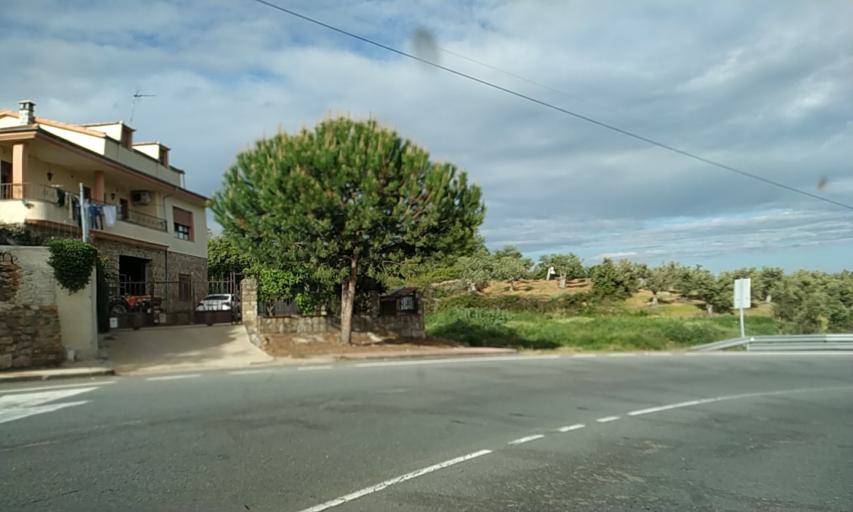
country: ES
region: Extremadura
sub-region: Provincia de Caceres
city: Perales del Puerto
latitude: 40.1541
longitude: -6.6798
